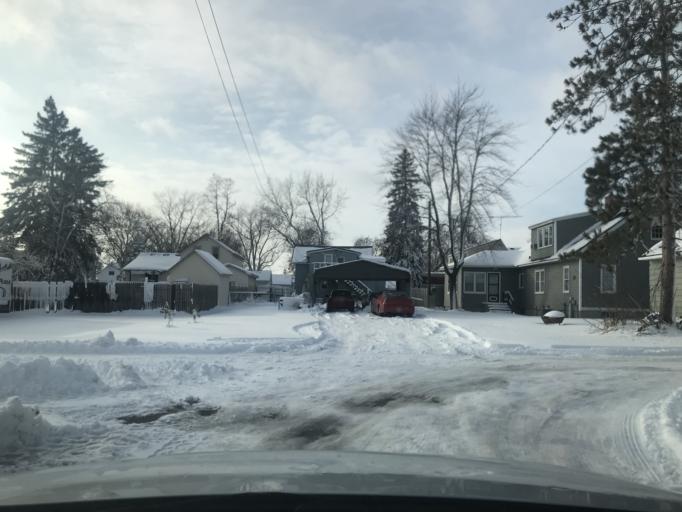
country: US
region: Wisconsin
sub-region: Marinette County
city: Peshtigo
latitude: 45.0524
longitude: -87.7500
